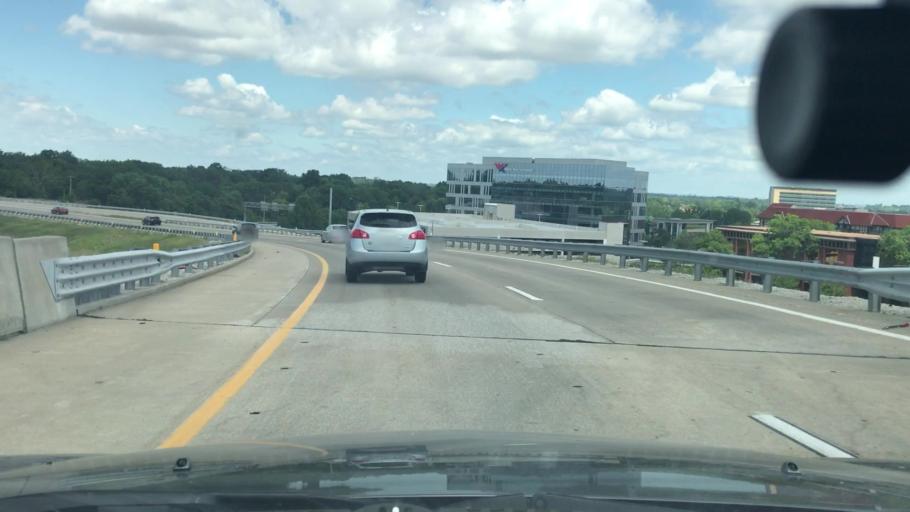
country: US
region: Missouri
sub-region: Saint Louis County
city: Maryland Heights
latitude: 38.6990
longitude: -90.4483
